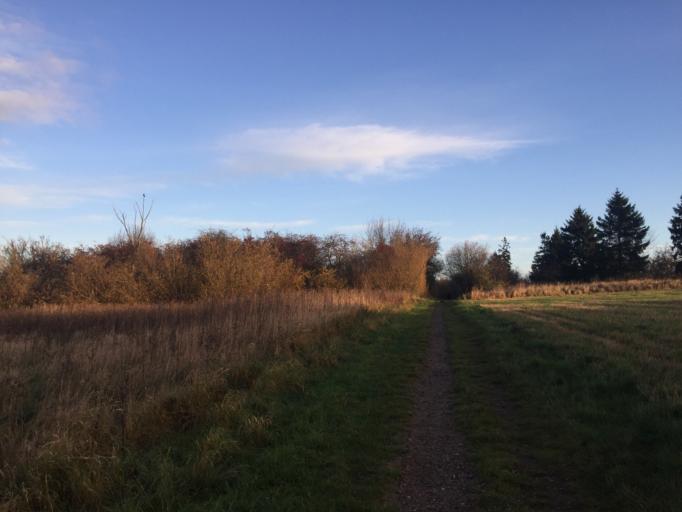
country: DK
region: Zealand
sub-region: Ringsted Kommune
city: Ringsted
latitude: 55.4281
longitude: 11.7753
